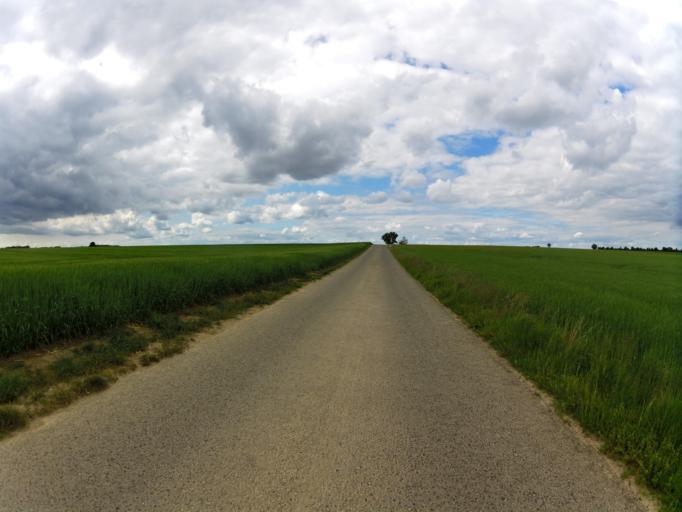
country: DE
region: Bavaria
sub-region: Regierungsbezirk Unterfranken
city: Gaukonigshofen
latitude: 49.6528
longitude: 10.0042
